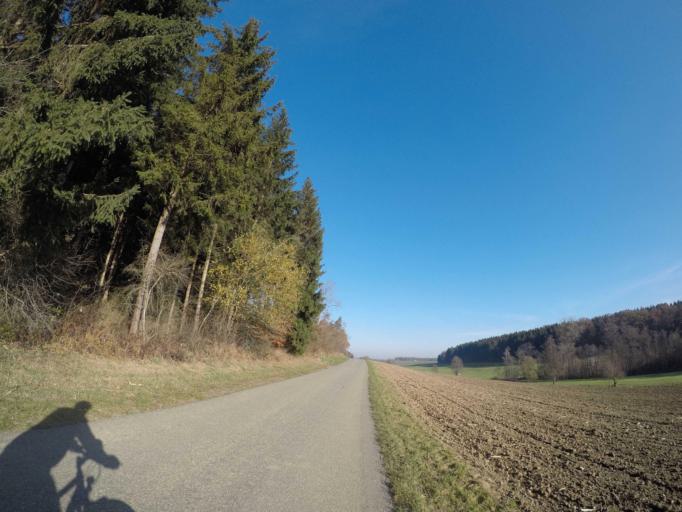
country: DE
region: Baden-Wuerttemberg
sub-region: Tuebingen Region
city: Unterwachingen
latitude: 48.1876
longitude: 9.6419
